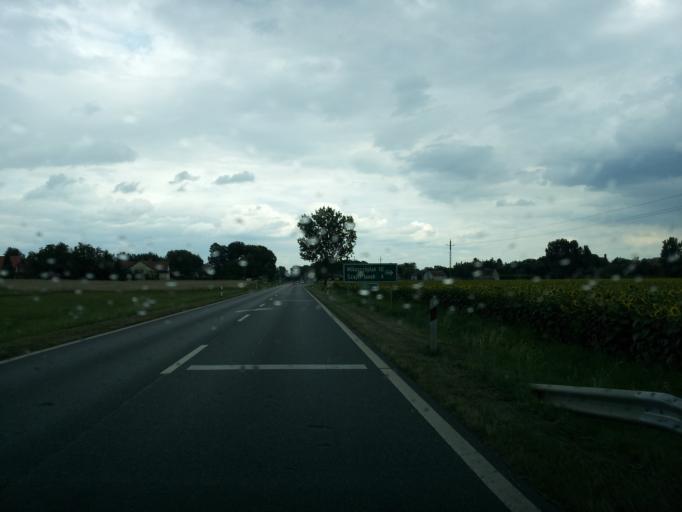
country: HU
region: Zala
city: Turje
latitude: 47.0961
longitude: 17.0159
